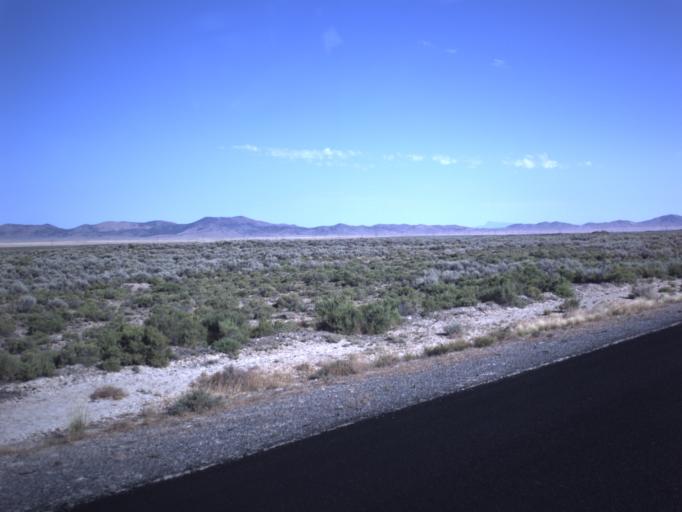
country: US
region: Utah
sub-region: Beaver County
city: Milford
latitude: 38.5345
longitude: -112.9912
